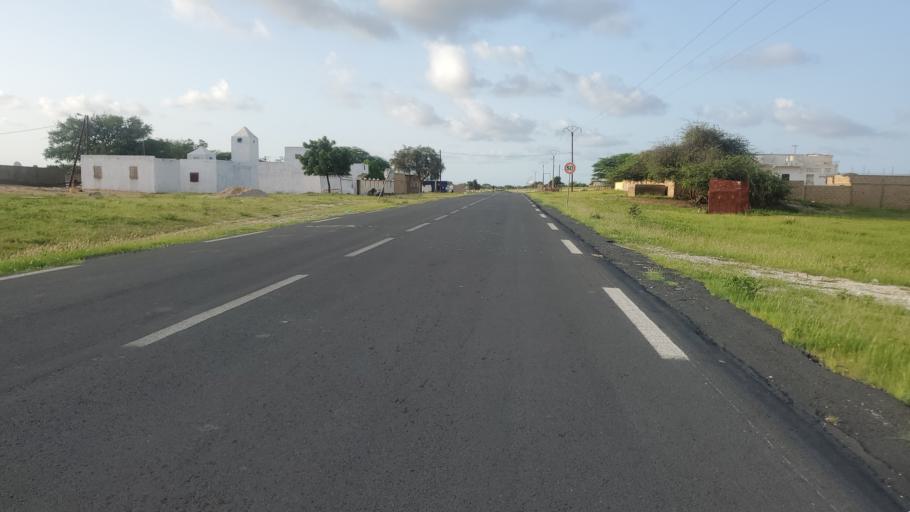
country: SN
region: Saint-Louis
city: Saint-Louis
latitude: 16.1524
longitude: -16.4098
